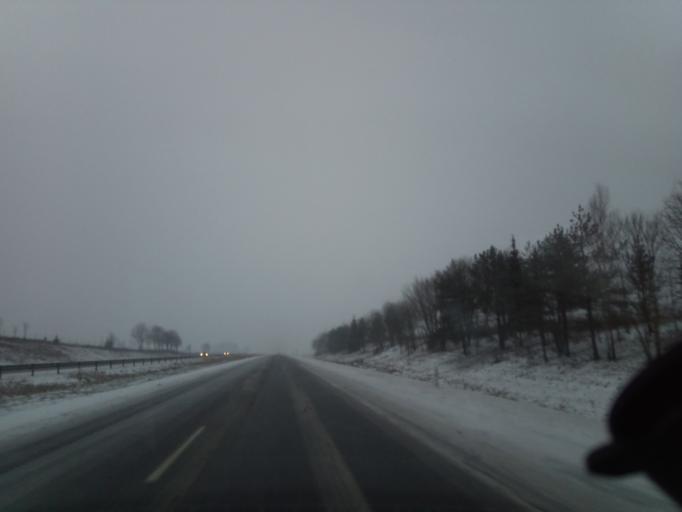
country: LT
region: Vilnius County
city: Pasilaiciai
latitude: 54.7883
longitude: 25.1750
